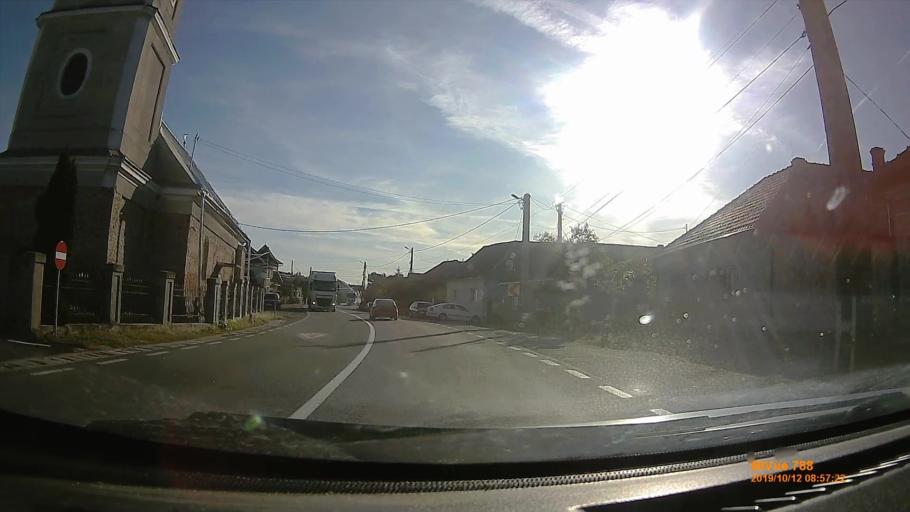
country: RO
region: Bihor
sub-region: Comuna Tileagd
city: Tileagd
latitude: 47.0807
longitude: 22.2145
